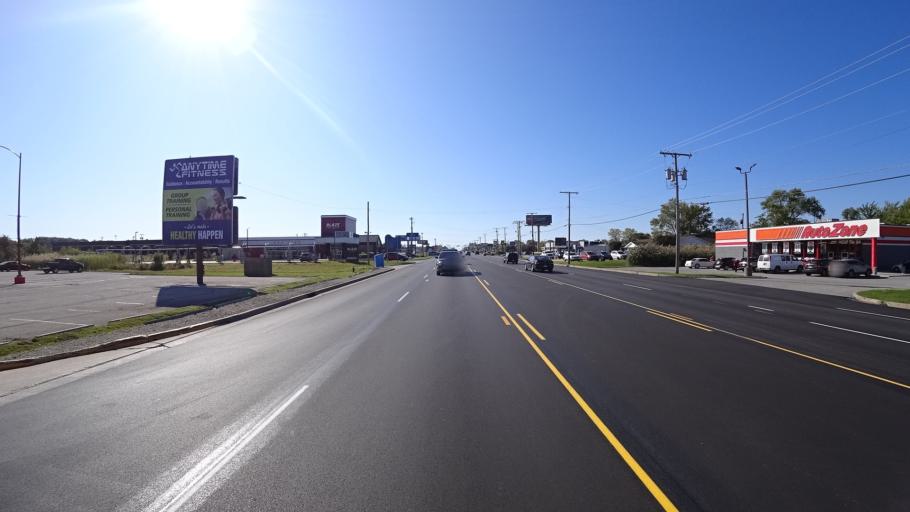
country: US
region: Indiana
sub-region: LaPorte County
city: Michigan City
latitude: 41.6781
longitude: -86.8939
